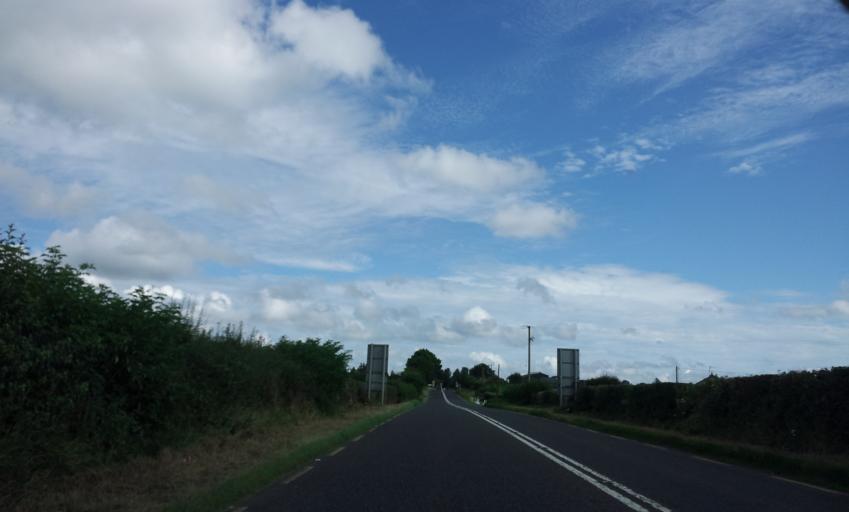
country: IE
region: Leinster
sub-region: Laois
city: Mountrath
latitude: 52.9886
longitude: -7.4880
